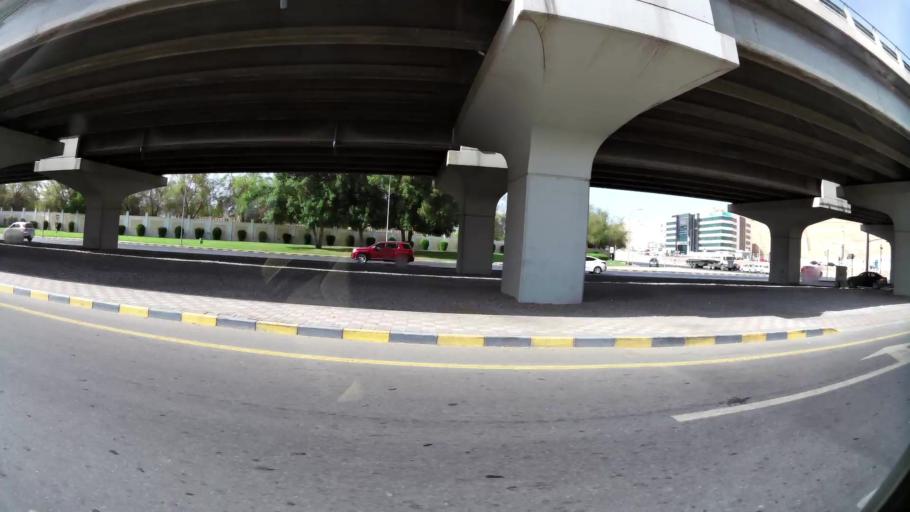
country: OM
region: Muhafazat Masqat
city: Muscat
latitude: 23.6067
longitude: 58.5106
